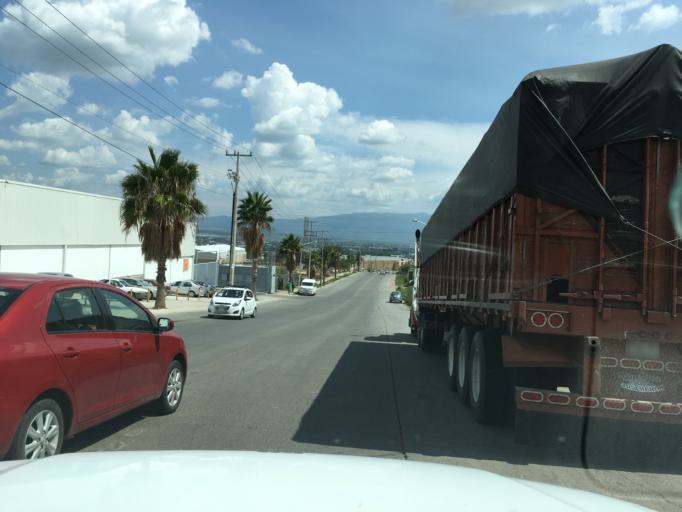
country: MX
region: Jalisco
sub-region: Tlajomulco de Zuniga
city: Altus Bosques
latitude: 20.5871
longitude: -103.3588
